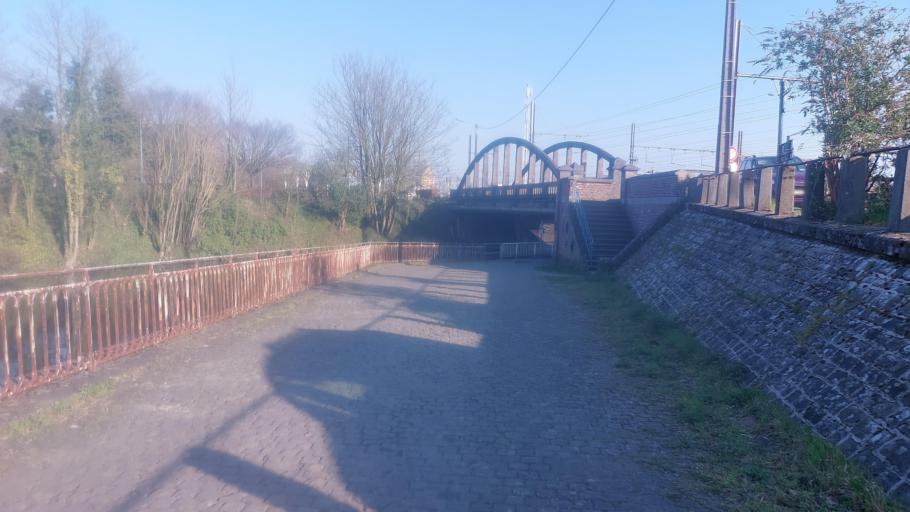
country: BE
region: Wallonia
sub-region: Province du Hainaut
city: Ath
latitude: 50.6278
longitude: 3.7714
